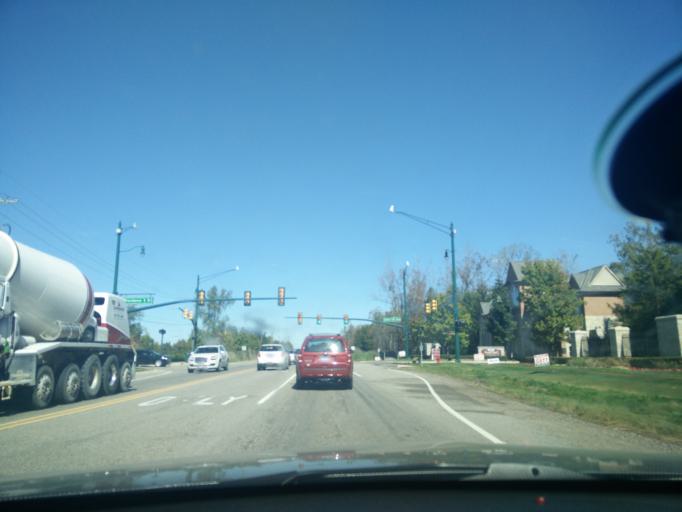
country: US
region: Michigan
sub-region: Oakland County
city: Novi
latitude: 42.4846
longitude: -83.5153
